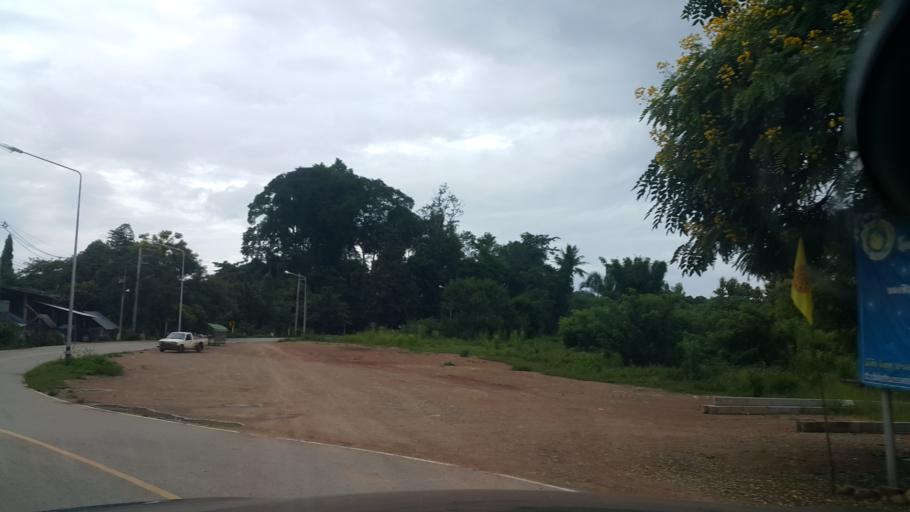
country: TH
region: Chiang Mai
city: San Sai
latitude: 18.9847
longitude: 99.1241
